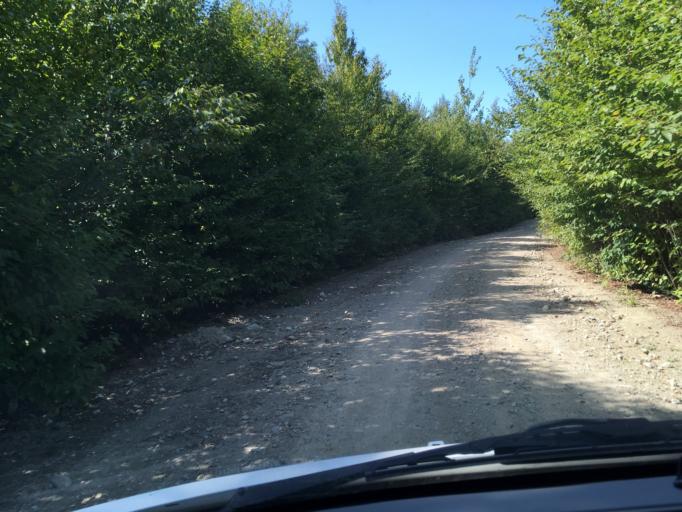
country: US
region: Maine
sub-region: Penobscot County
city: Millinocket
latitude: 45.8572
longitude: -68.7539
